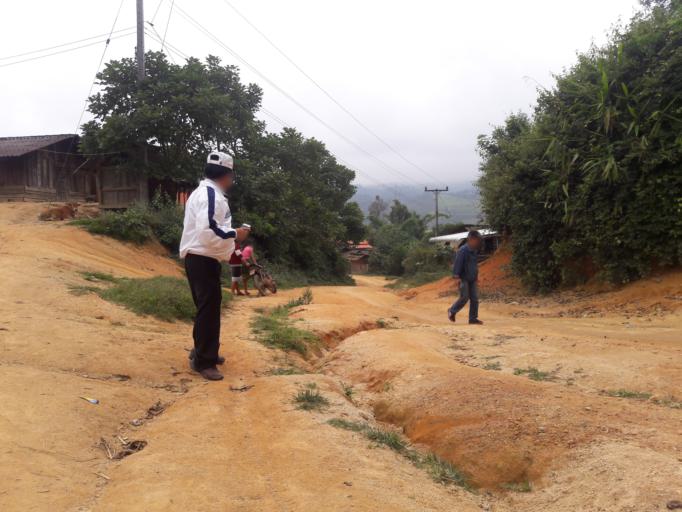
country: LA
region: Xiangkhoang
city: Muang Phonsavan
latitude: 19.3354
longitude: 103.4930
